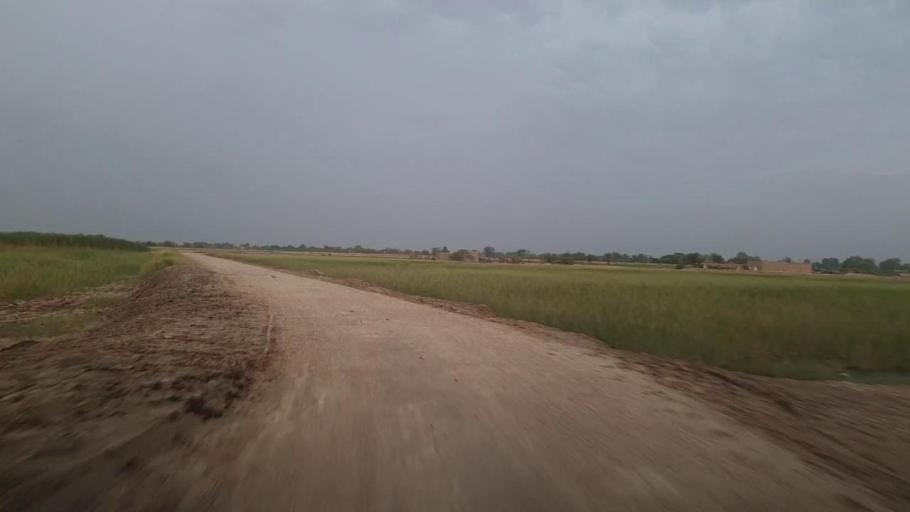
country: PK
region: Sindh
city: Karaundi
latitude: 27.0007
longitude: 68.3474
